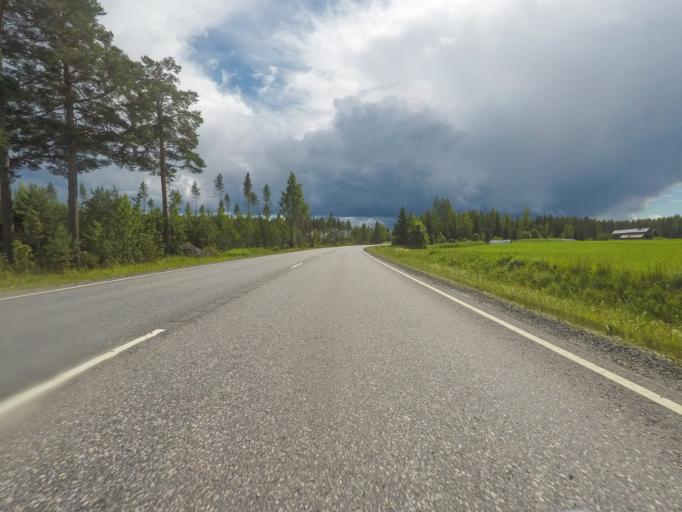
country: FI
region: Central Finland
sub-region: Joutsa
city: Joutsa
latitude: 61.6932
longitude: 26.0590
